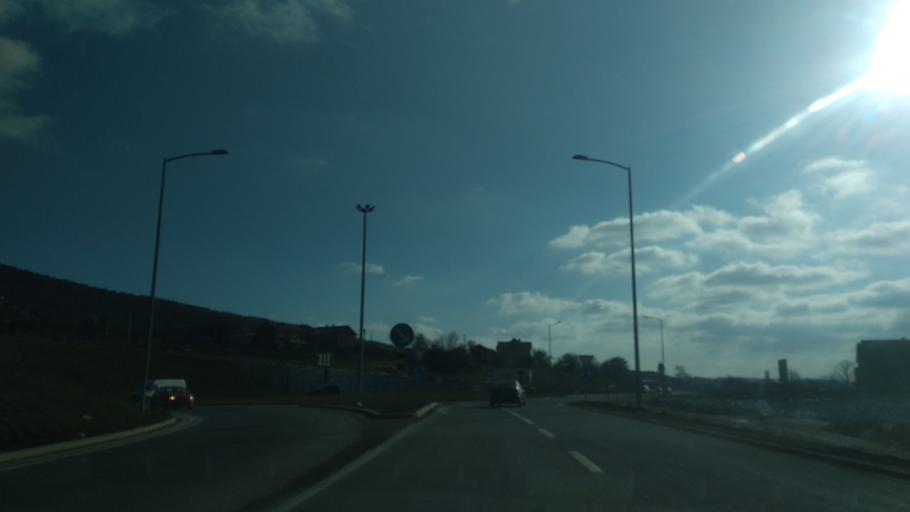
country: XK
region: Pristina
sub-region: Komuna e Prishtines
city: Pristina
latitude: 42.7327
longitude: 21.1423
